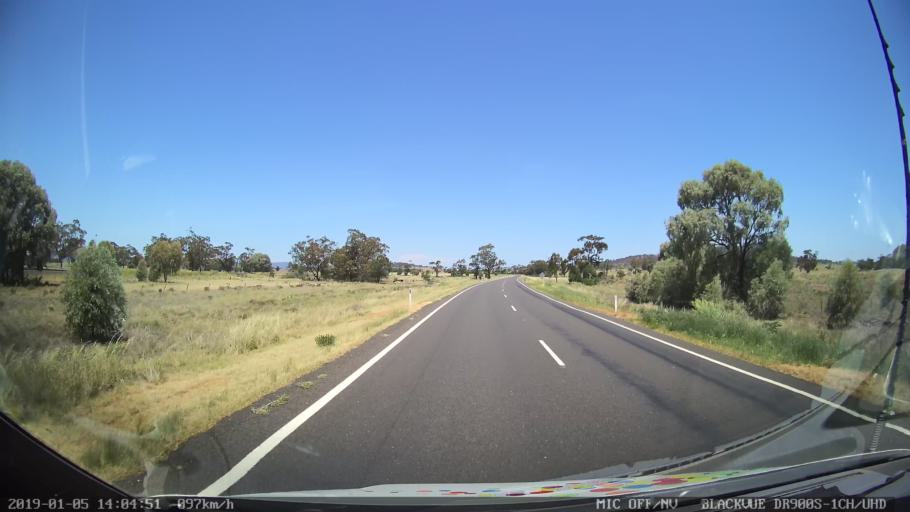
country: AU
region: New South Wales
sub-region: Gunnedah
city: Gunnedah
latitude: -31.2042
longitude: 150.3689
